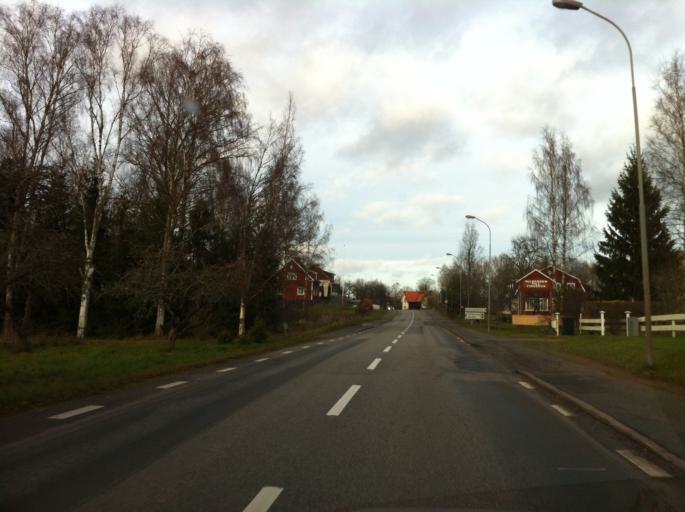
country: SE
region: Kronoberg
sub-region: Uppvidinge Kommun
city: Aseda
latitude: 57.1814
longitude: 15.4994
